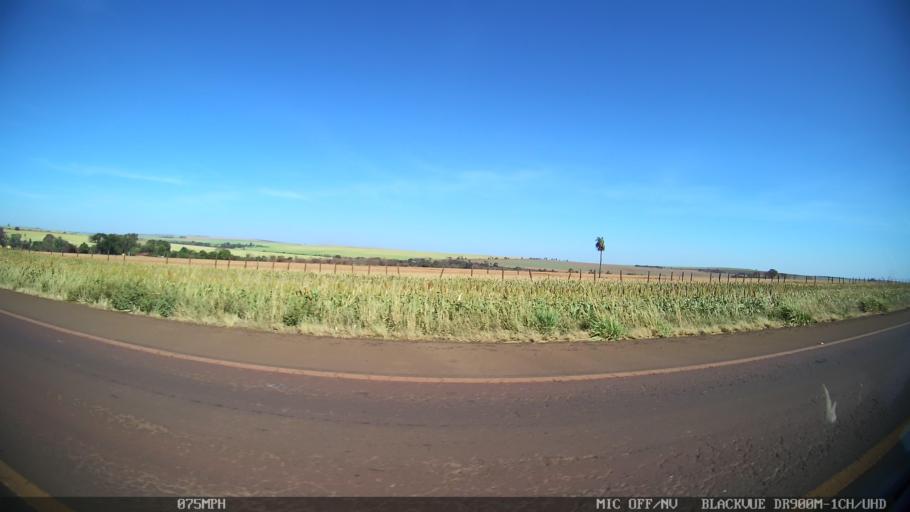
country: BR
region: Sao Paulo
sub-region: Ipua
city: Ipua
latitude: -20.4582
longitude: -48.1519
